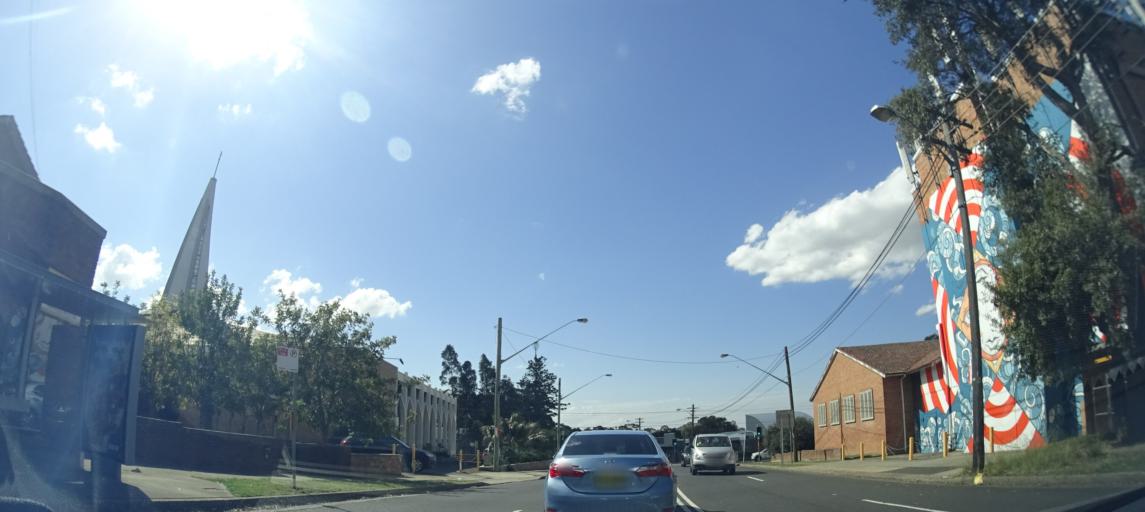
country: AU
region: New South Wales
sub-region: Bankstown
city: Revesby
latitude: -33.9459
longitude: 151.0178
